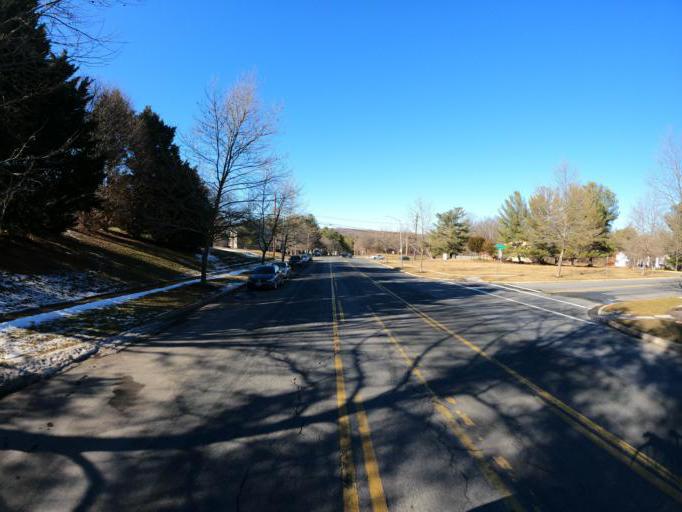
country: US
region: Maryland
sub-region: Montgomery County
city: Montgomery Village
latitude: 39.1836
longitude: -77.2320
